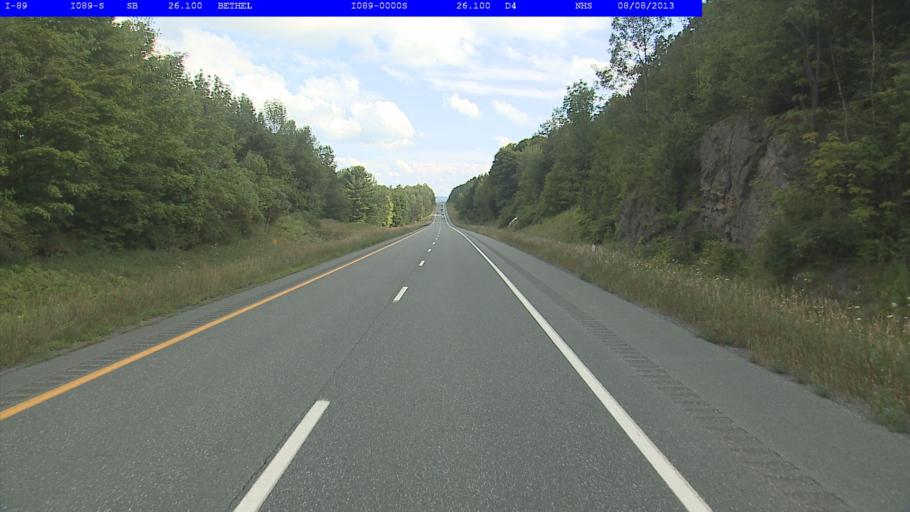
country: US
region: Vermont
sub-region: Orange County
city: Randolph
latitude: 43.8772
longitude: -72.6153
